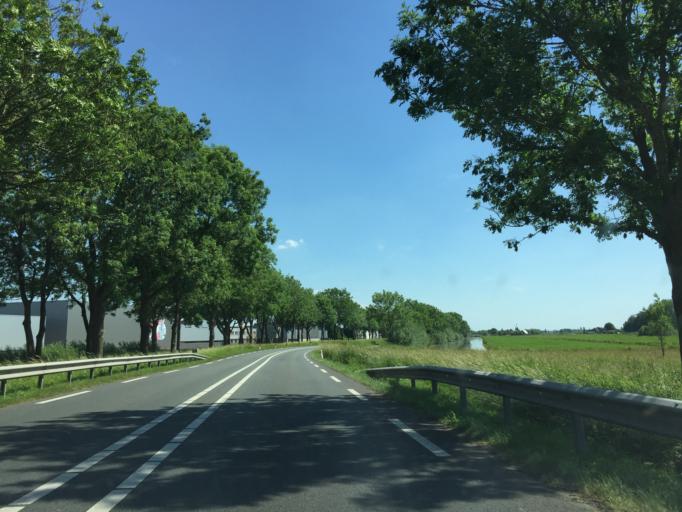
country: NL
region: South Holland
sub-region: Gemeente Vlist
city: Haastrecht
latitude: 51.9676
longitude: 4.7715
